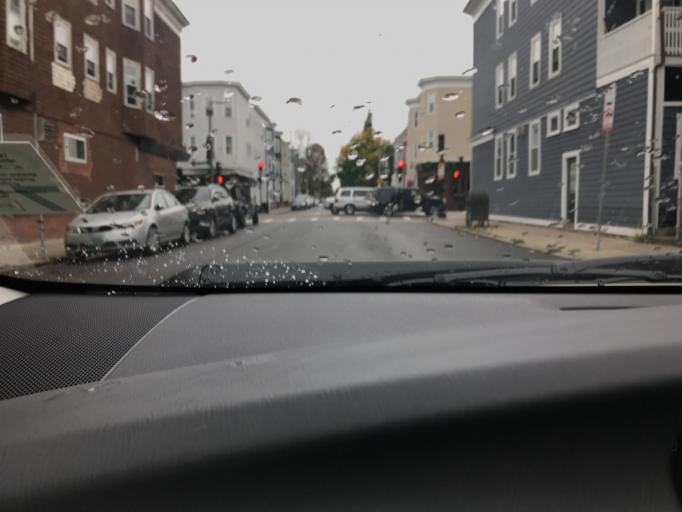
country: US
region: Massachusetts
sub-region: Suffolk County
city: South Boston
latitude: 42.3315
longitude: -71.0347
